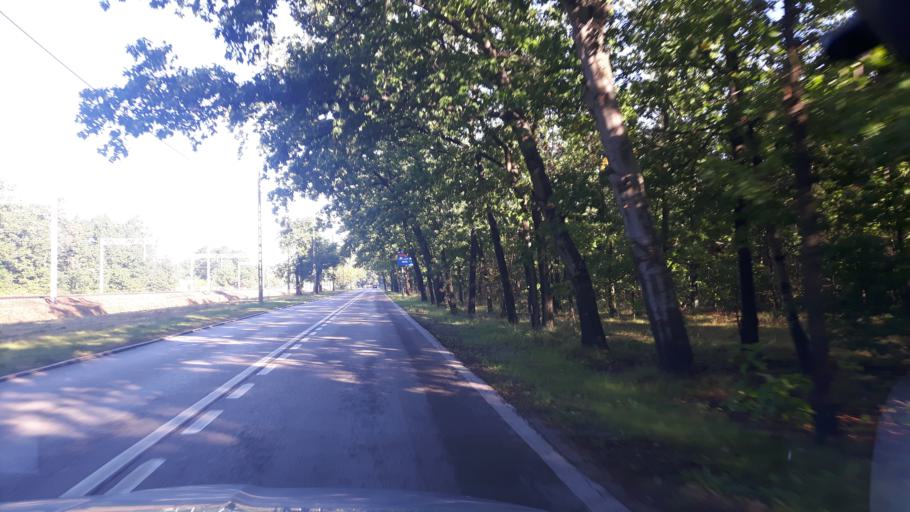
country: PL
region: Masovian Voivodeship
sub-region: Warszawa
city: Bialoleka
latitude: 52.3455
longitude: 20.9800
